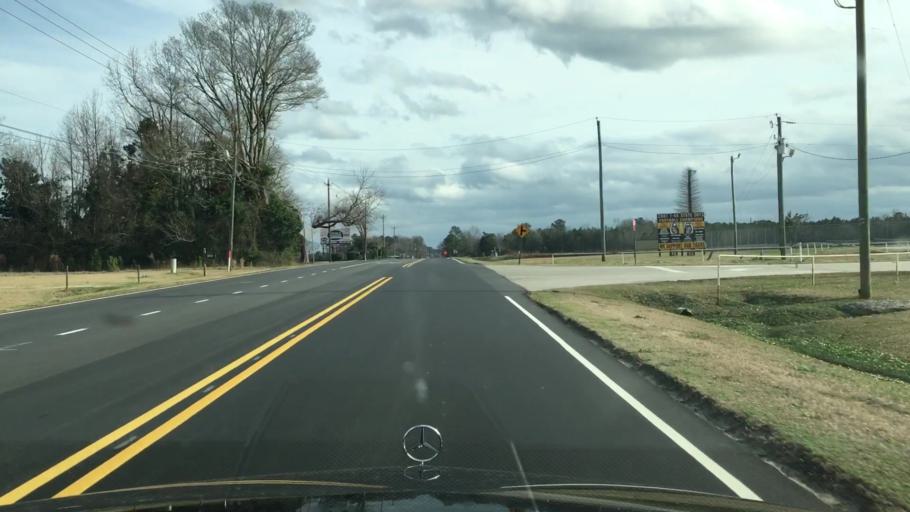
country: US
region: North Carolina
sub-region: Duplin County
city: Warsaw
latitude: 34.9848
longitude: -78.0416
